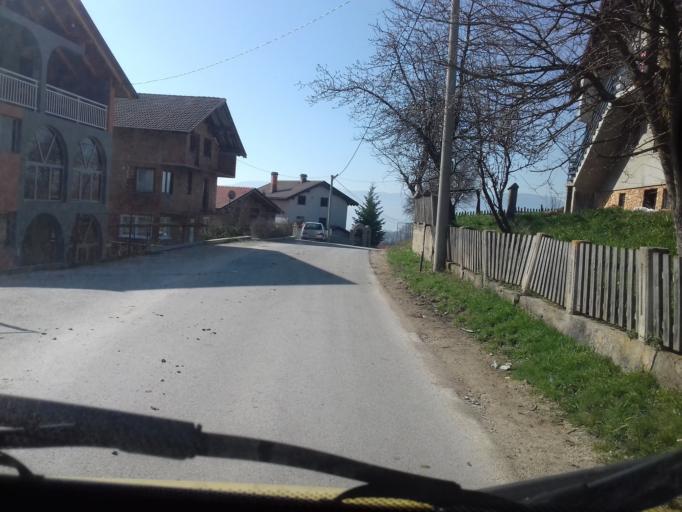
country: BA
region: Federation of Bosnia and Herzegovina
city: Travnik
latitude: 44.2512
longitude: 17.7355
